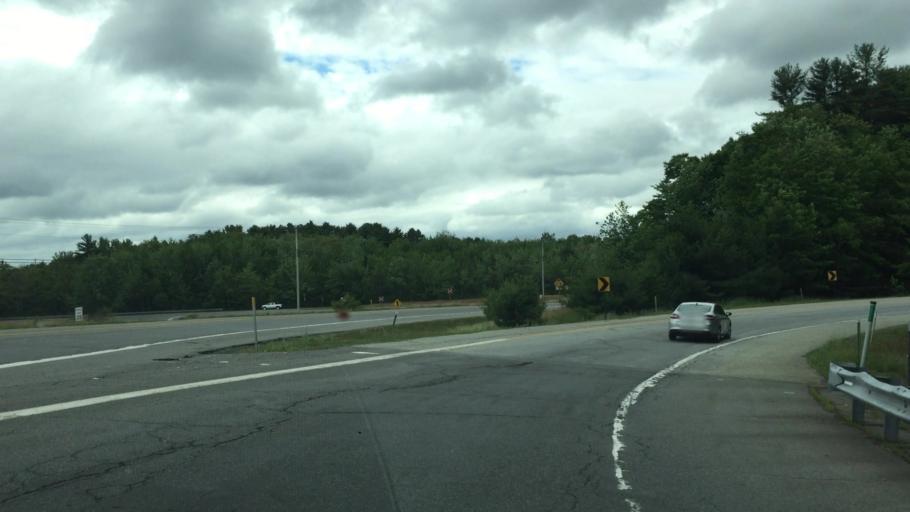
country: US
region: Maine
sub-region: Cumberland County
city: Falmouth
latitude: 43.7301
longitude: -70.2301
